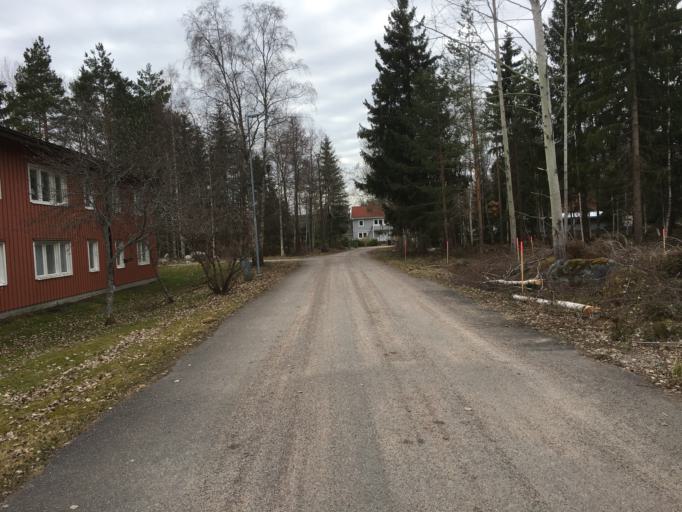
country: SE
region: Gaevleborg
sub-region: Hofors Kommun
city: Hofors
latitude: 60.5146
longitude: 16.4685
